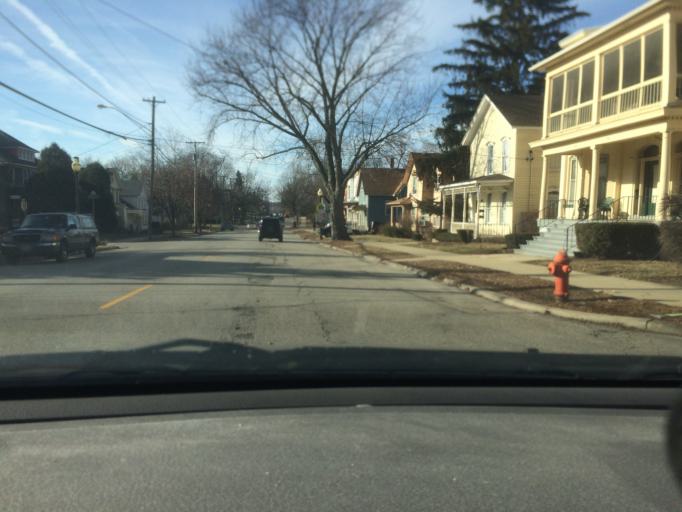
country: US
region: Illinois
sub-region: Kane County
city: Elgin
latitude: 42.0371
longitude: -88.2704
